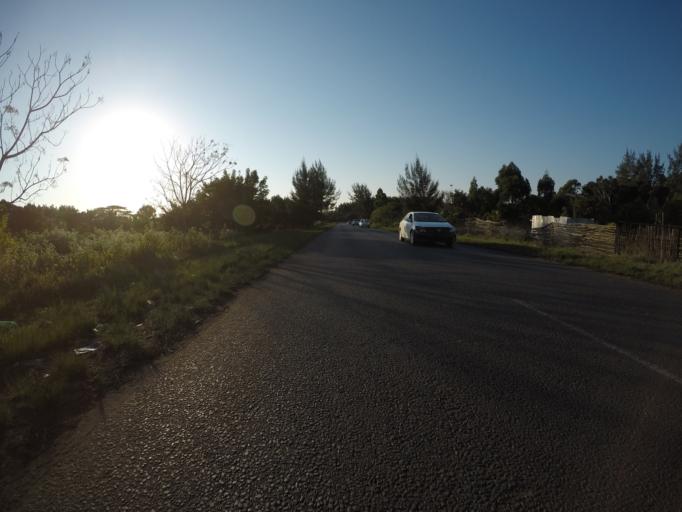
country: ZA
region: KwaZulu-Natal
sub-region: uThungulu District Municipality
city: KwaMbonambi
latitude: -28.6846
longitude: 32.2059
